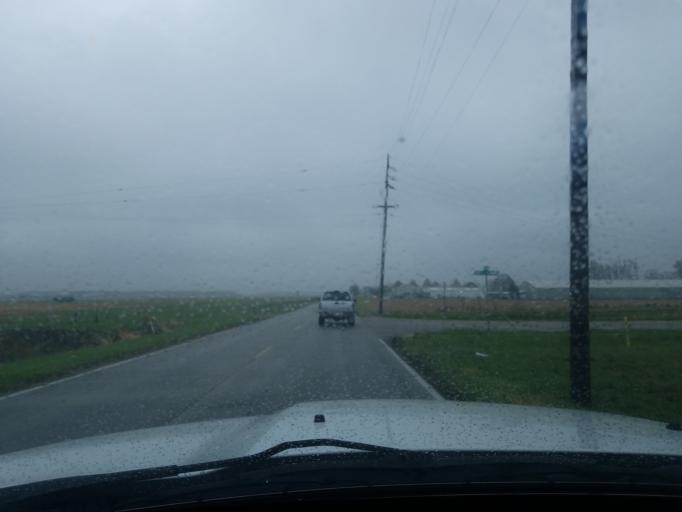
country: US
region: Indiana
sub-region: Delaware County
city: Muncie
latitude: 40.2335
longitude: -85.4005
